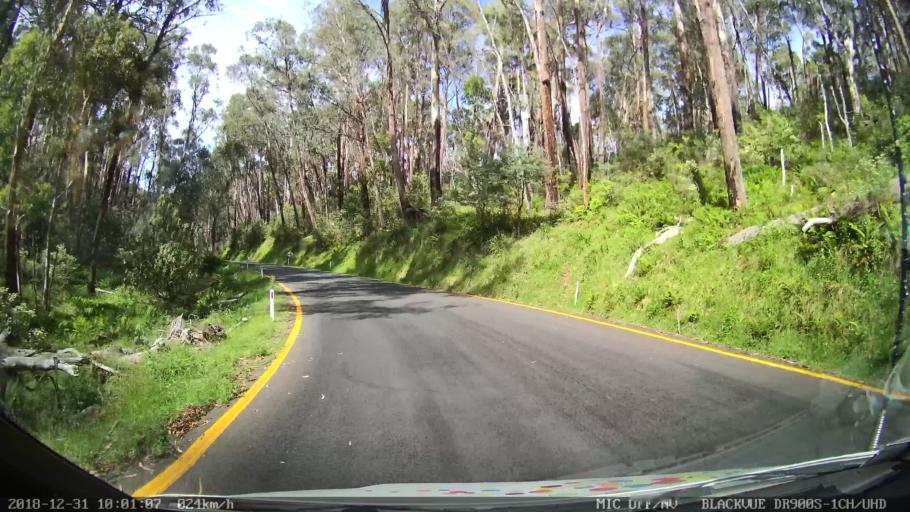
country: AU
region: New South Wales
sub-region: Snowy River
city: Jindabyne
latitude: -36.5295
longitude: 148.2042
